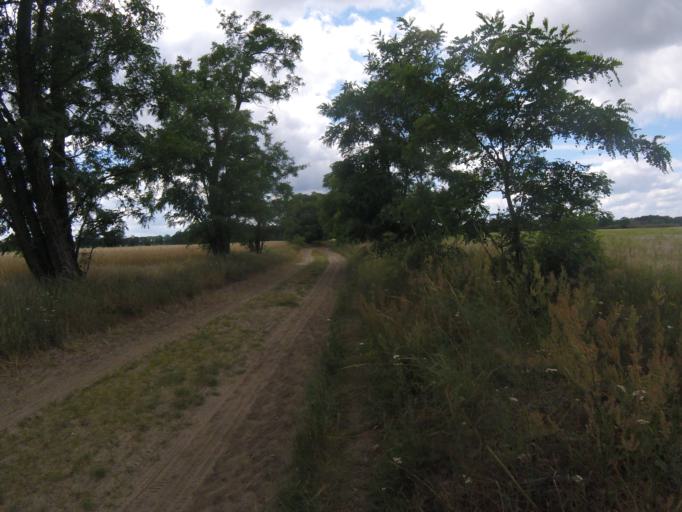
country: DE
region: Brandenburg
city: Mittenwalde
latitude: 52.2528
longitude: 13.5764
